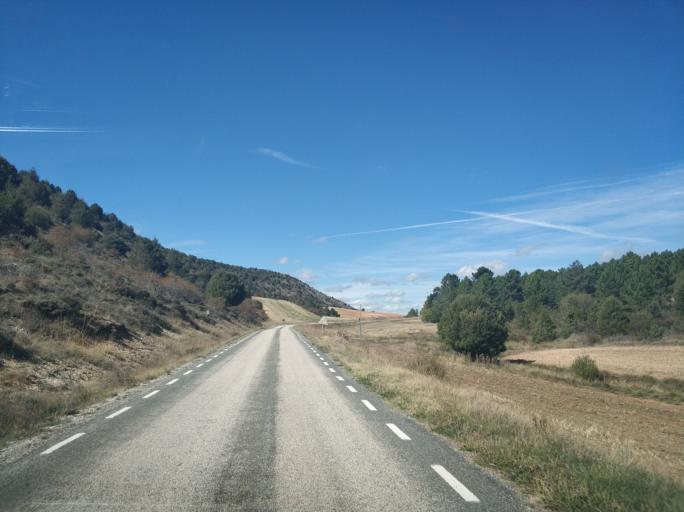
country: ES
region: Castille and Leon
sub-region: Provincia de Soria
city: Espeja de San Marcelino
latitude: 41.8163
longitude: -3.2349
